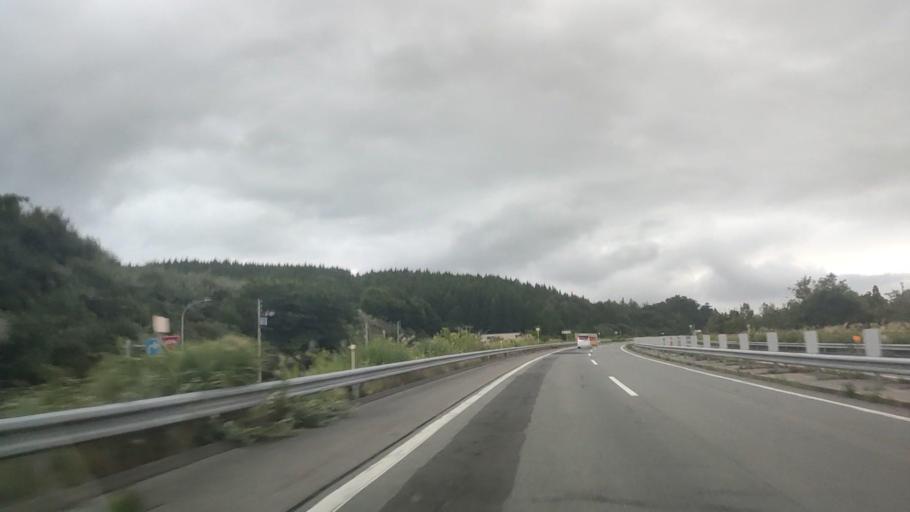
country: JP
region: Hokkaido
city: Nanae
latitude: 41.8998
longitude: 140.7045
